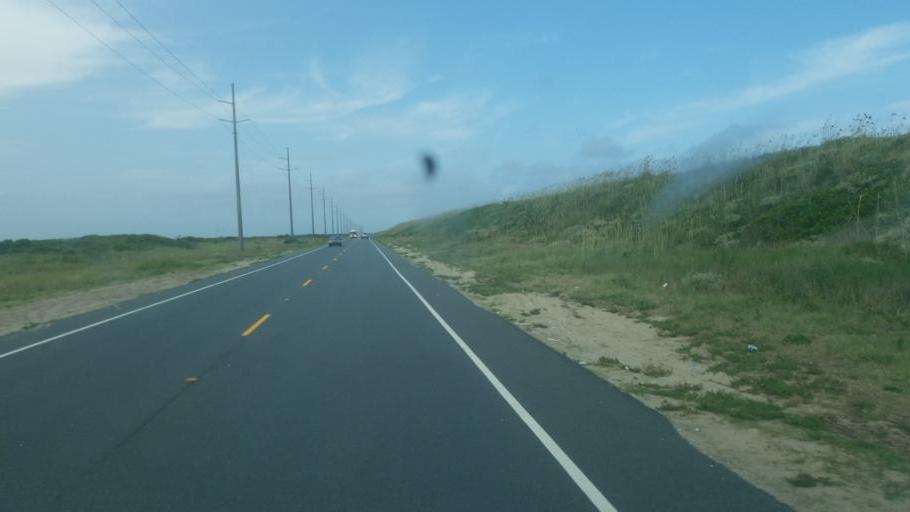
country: US
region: North Carolina
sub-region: Dare County
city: Buxton
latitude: 35.2770
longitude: -75.5176
